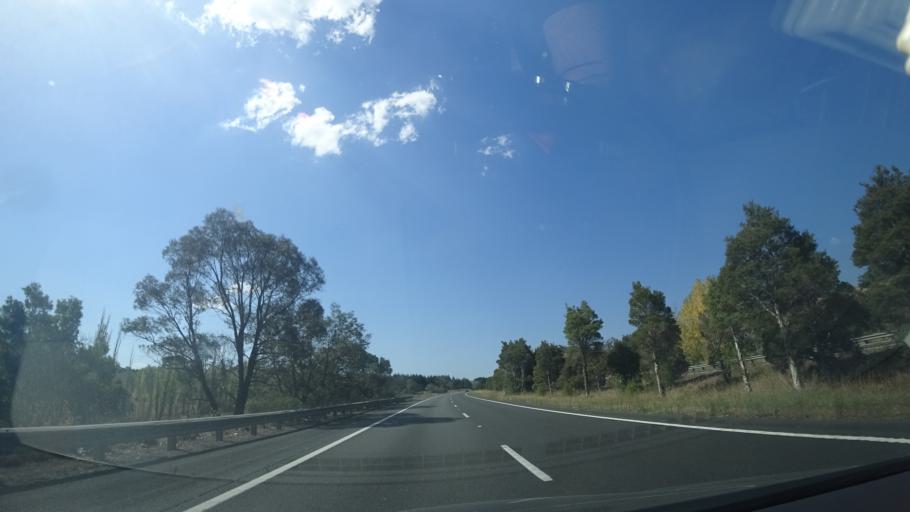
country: AU
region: New South Wales
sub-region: Wingecarribee
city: Bundanoon
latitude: -34.5652
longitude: 150.2546
